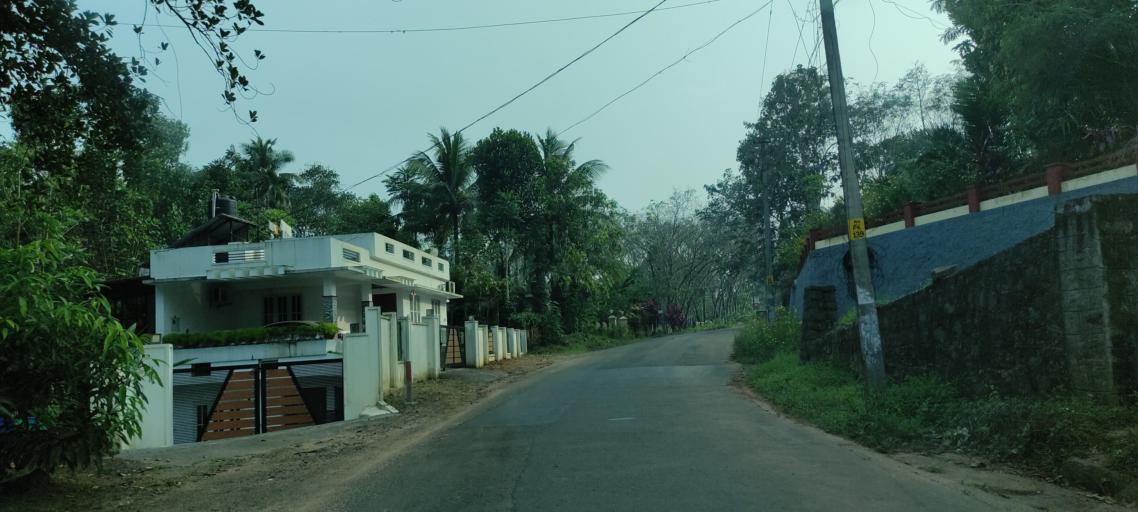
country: IN
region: Kerala
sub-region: Ernakulam
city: Piravam
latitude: 9.7931
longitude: 76.4995
